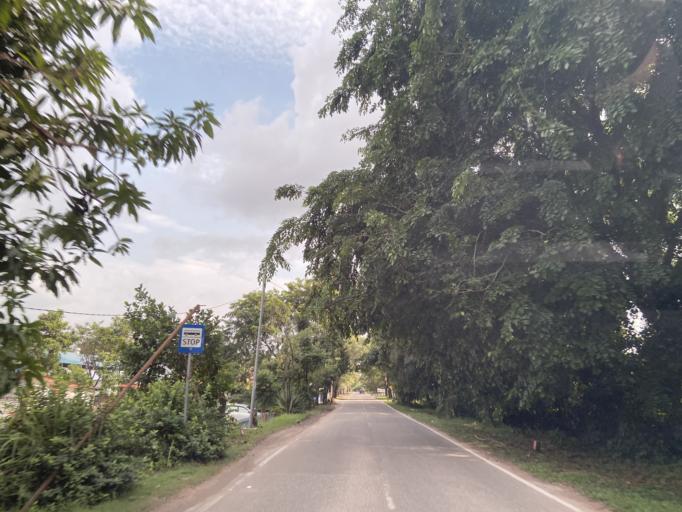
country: SG
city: Singapore
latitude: 1.1192
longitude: 104.0202
